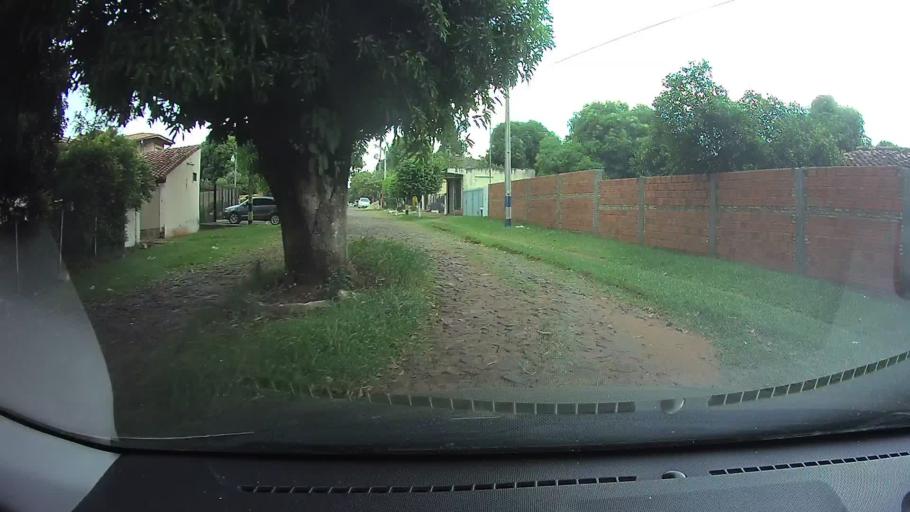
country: PY
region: Central
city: San Lorenzo
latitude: -25.2817
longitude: -57.4934
